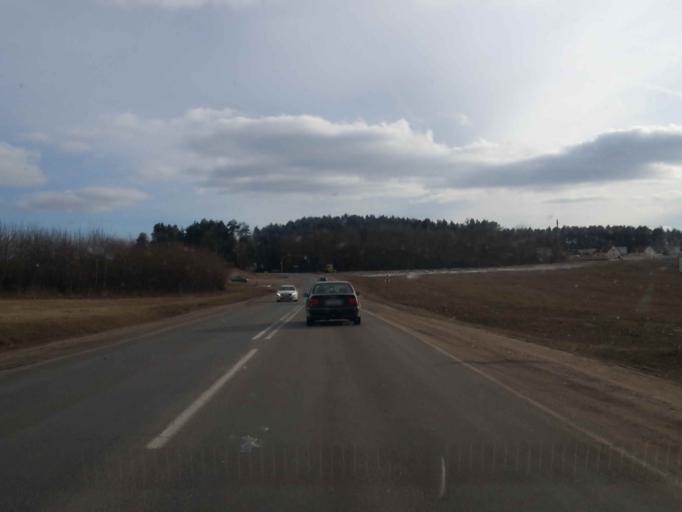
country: BY
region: Minsk
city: Bal'shavik
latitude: 54.0320
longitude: 27.5597
